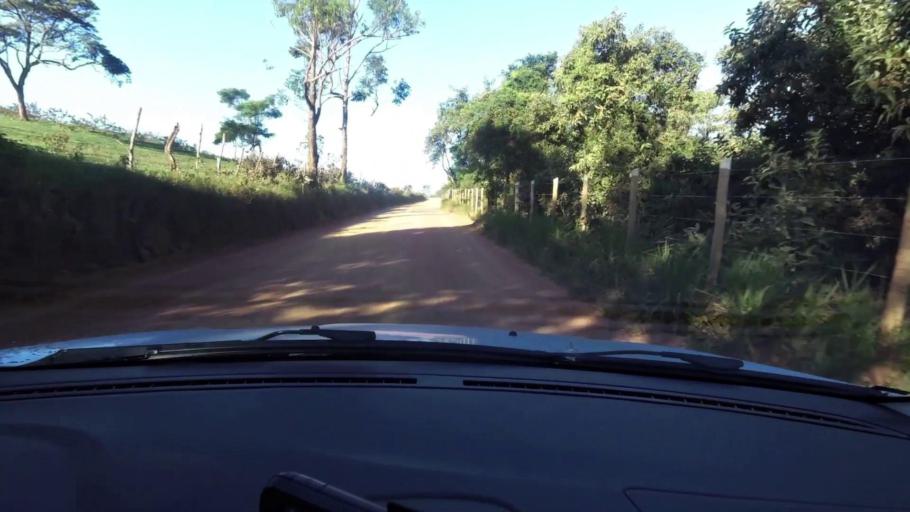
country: BR
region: Espirito Santo
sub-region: Guarapari
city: Guarapari
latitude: -20.7237
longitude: -40.5860
